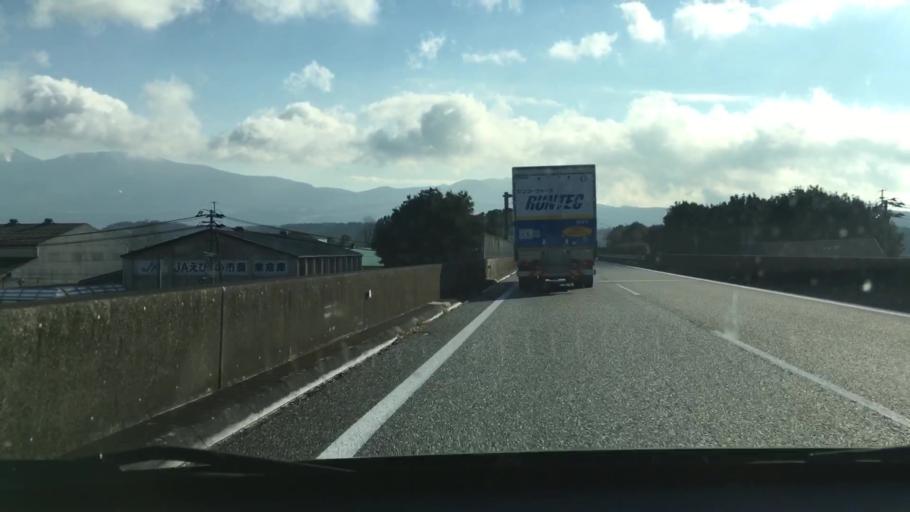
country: JP
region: Kumamoto
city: Hitoyoshi
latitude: 32.0535
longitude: 130.8020
